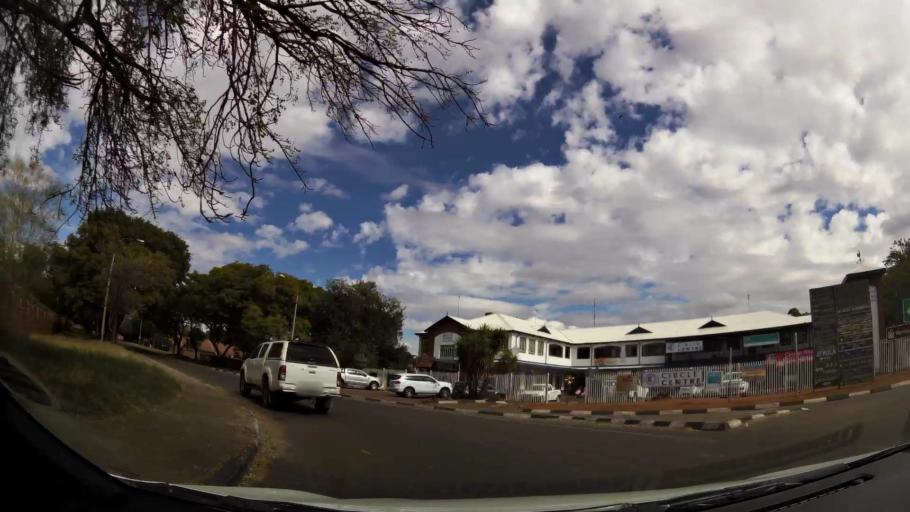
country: ZA
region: Limpopo
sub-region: Waterberg District Municipality
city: Warmbaths
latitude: -24.8858
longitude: 28.2845
